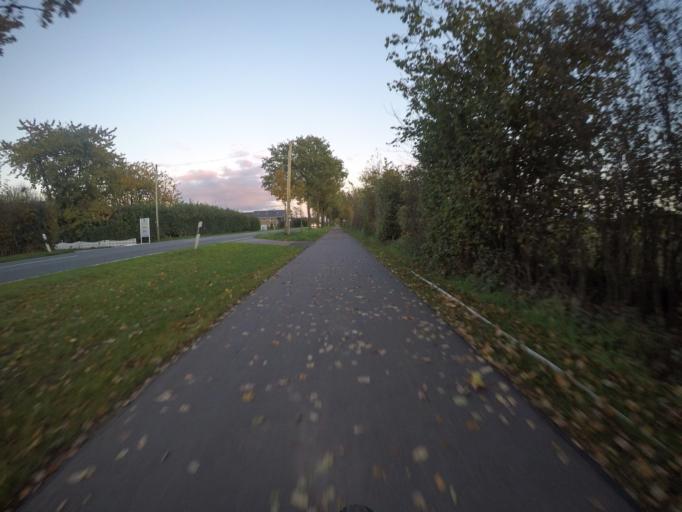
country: DE
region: North Rhine-Westphalia
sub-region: Regierungsbezirk Dusseldorf
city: Bocholt
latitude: 51.8438
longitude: 6.5457
